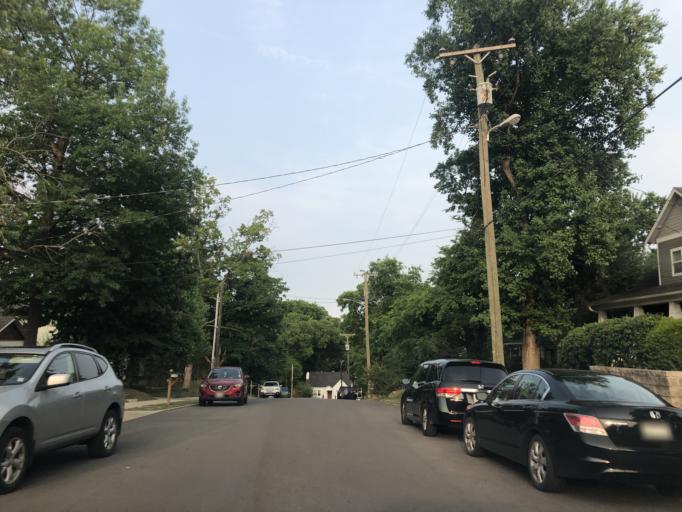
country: US
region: Tennessee
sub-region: Davidson County
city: Oak Hill
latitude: 36.1254
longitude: -86.7848
